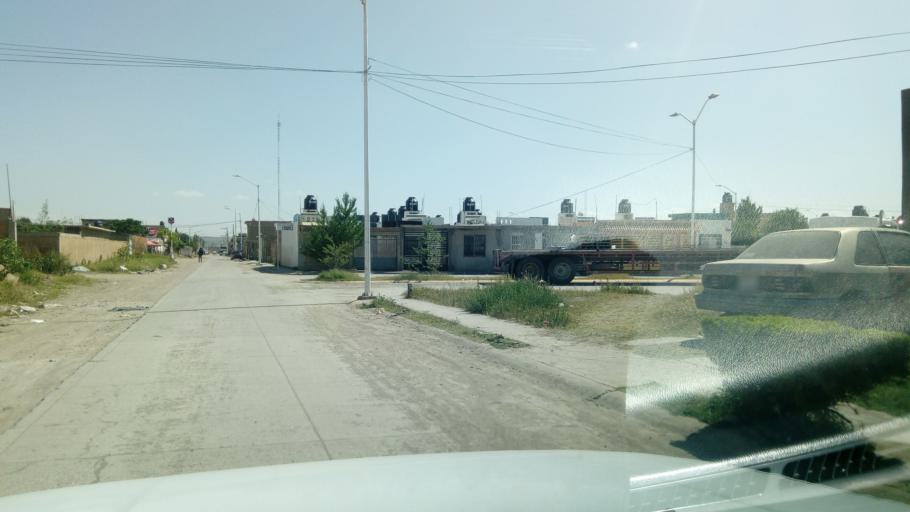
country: MX
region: Durango
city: Victoria de Durango
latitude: 23.9956
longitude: -104.6946
